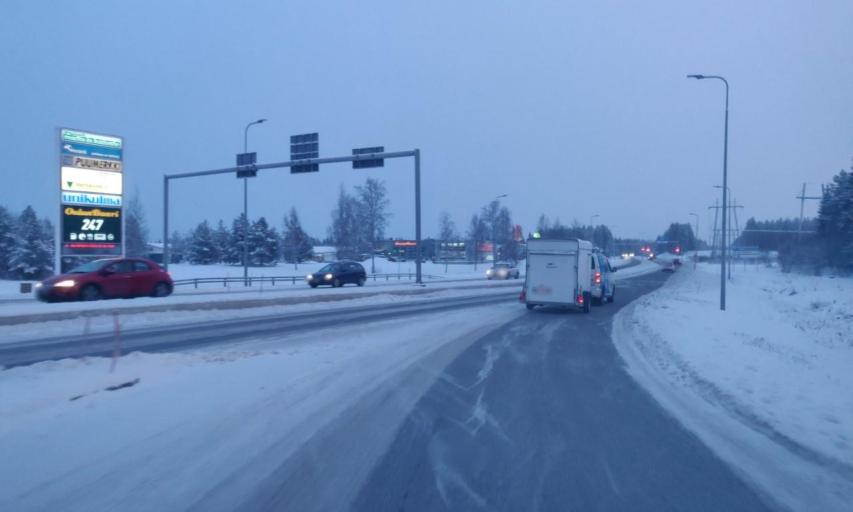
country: FI
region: Northern Ostrobothnia
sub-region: Oulu
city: Kempele
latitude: 64.9806
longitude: 25.5607
